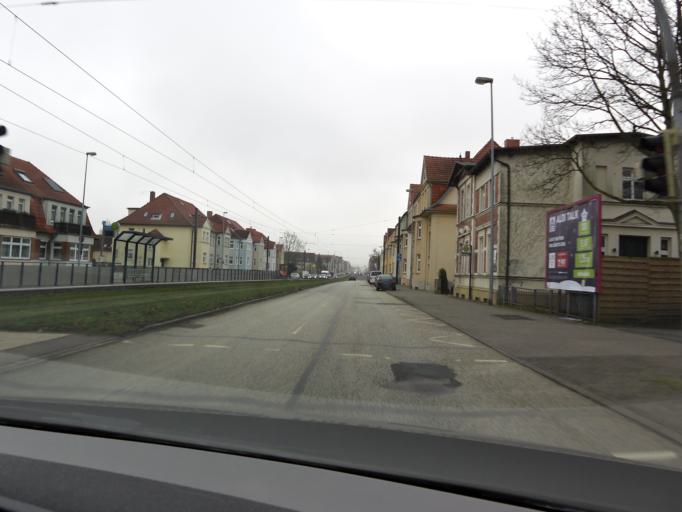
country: DE
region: Mecklenburg-Vorpommern
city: Weststadt
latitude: 53.6415
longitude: 11.3899
